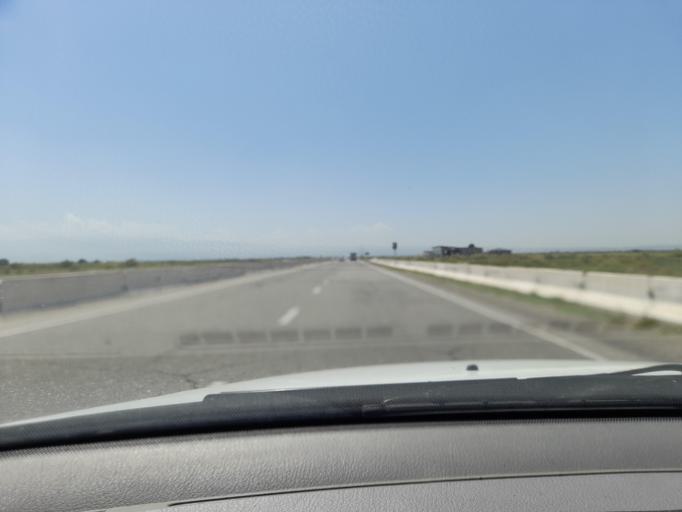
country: UZ
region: Jizzax
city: Paxtakor
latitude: 40.2093
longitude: 67.9833
